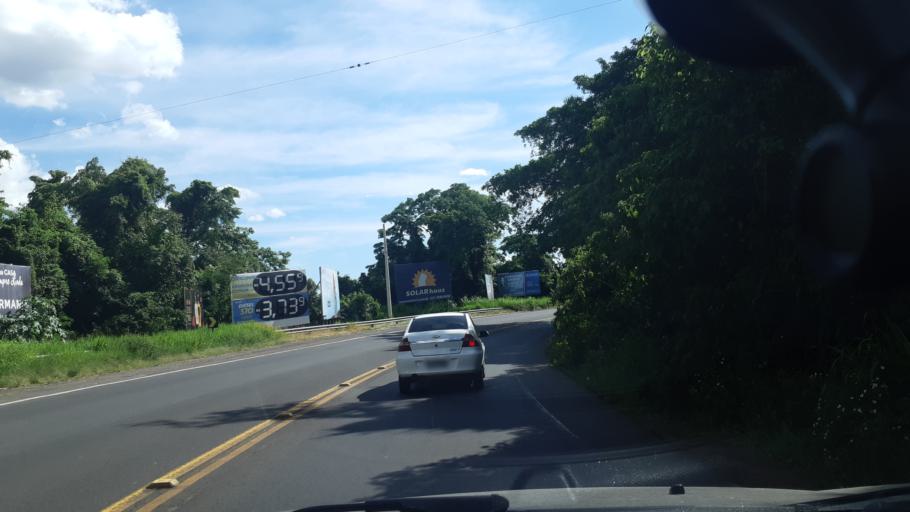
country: BR
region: Rio Grande do Sul
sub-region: Estancia Velha
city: Estancia Velha
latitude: -29.6278
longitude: -51.1389
